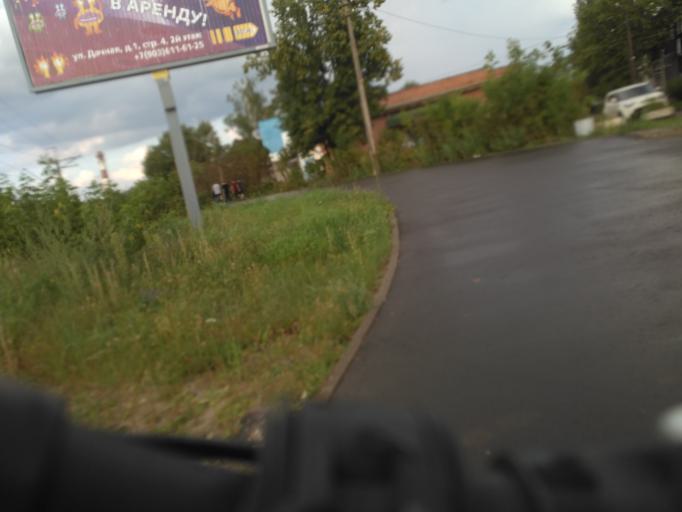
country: RU
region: Moskovskaya
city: Dubna
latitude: 56.7436
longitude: 37.1788
